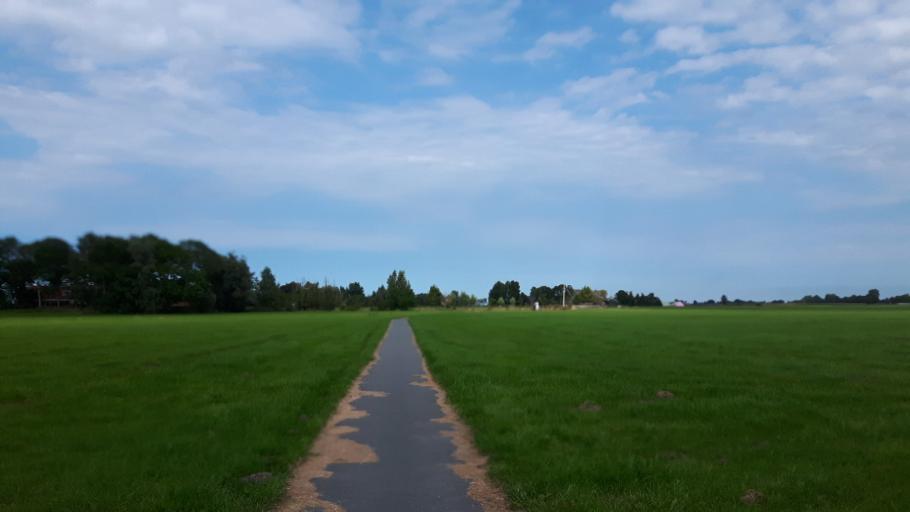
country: NL
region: Friesland
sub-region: Gemeente Leeuwarden
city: Camminghaburen
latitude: 53.2329
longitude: 5.8253
